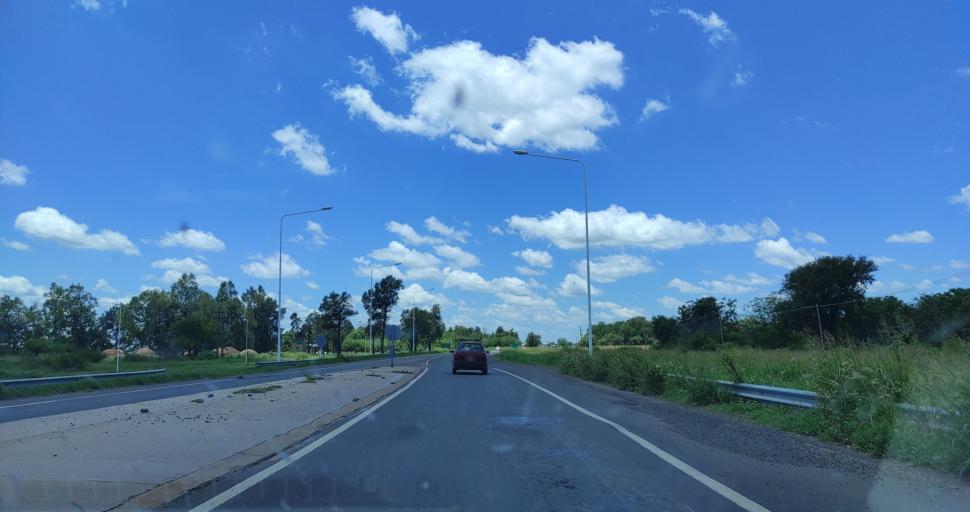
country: AR
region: Chaco
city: Avia Terai
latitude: -26.7039
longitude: -60.7269
